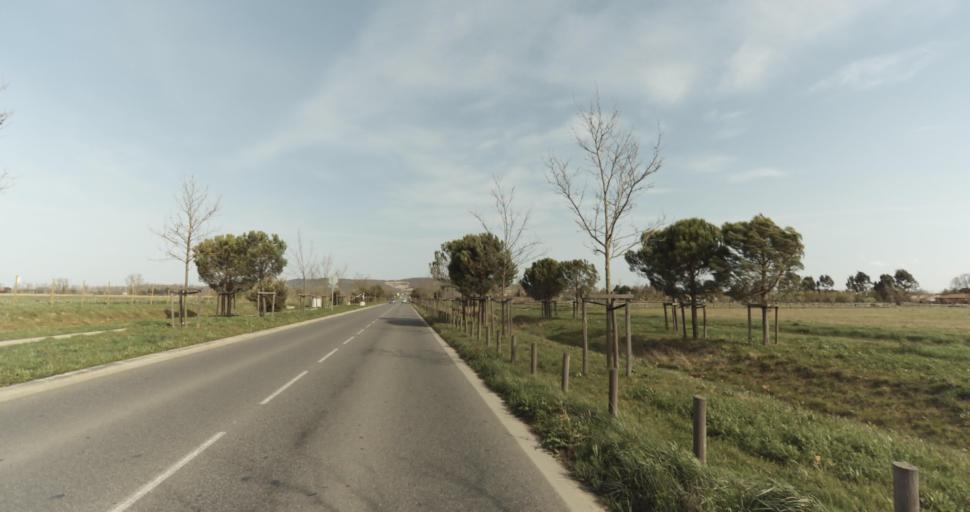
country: FR
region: Midi-Pyrenees
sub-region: Departement du Tarn
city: Saint-Sulpice-la-Pointe
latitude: 43.7594
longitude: 1.6584
